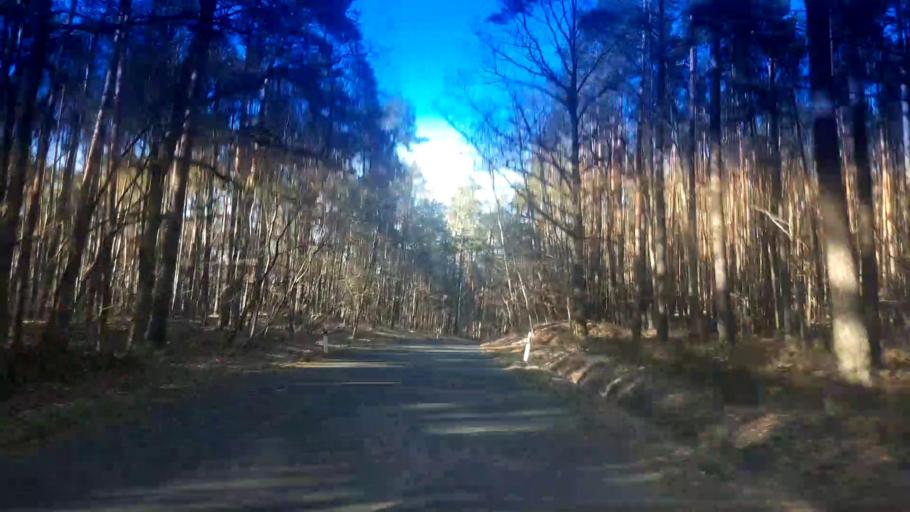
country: DE
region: Bavaria
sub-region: Upper Franconia
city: Lauter
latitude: 49.9608
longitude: 10.7617
